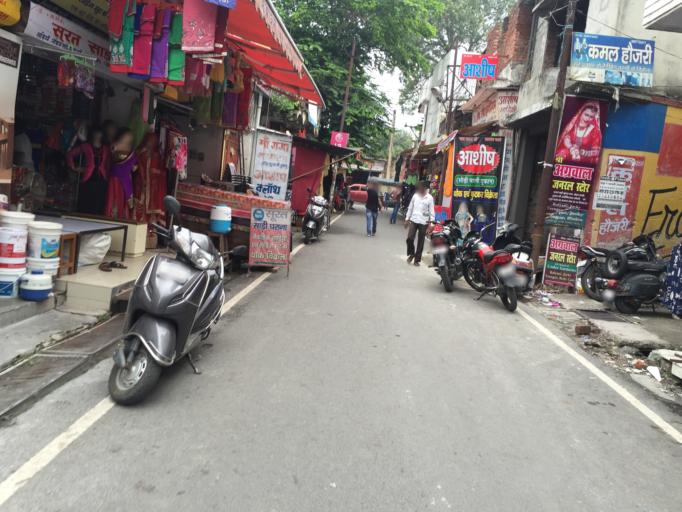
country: IN
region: Uttarakhand
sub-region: Dehradun
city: Rishikesh
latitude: 30.1053
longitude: 78.2994
